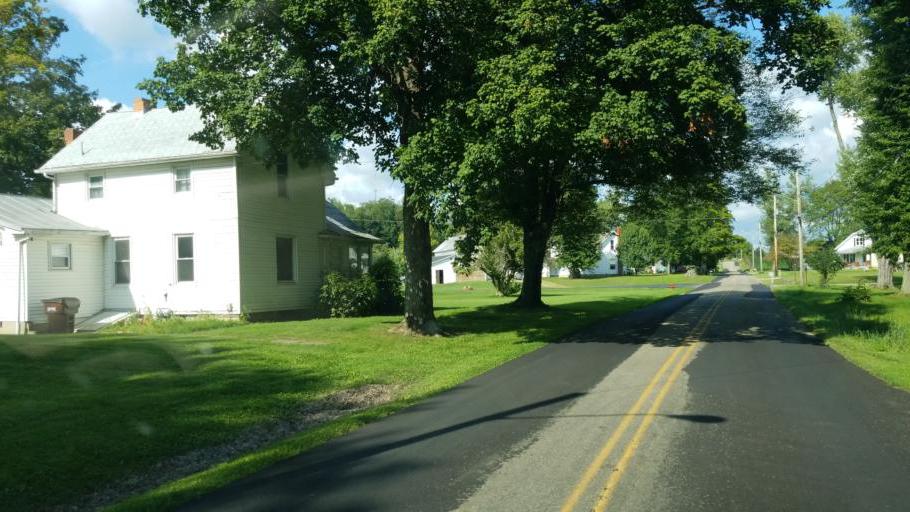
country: US
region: Ohio
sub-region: Knox County
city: Danville
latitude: 40.4130
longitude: -82.3237
